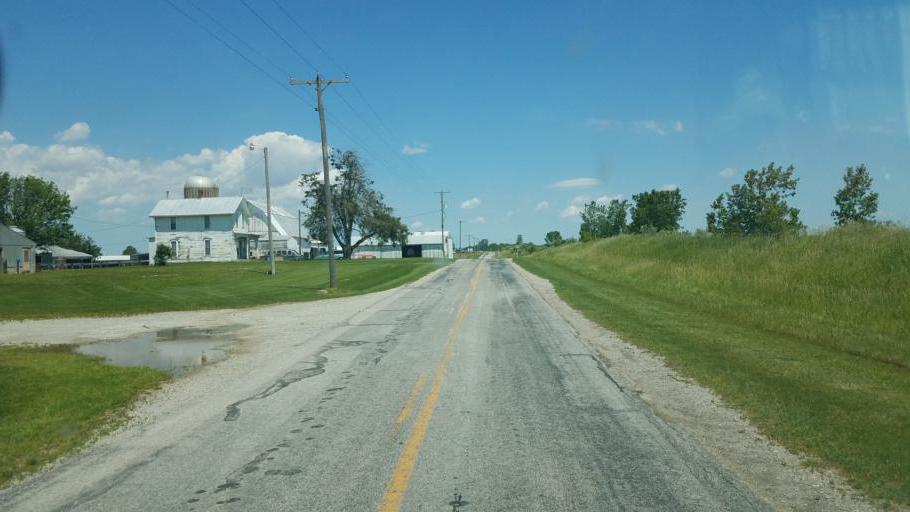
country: US
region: Ohio
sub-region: Hardin County
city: Forest
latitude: 40.6774
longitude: -83.4197
